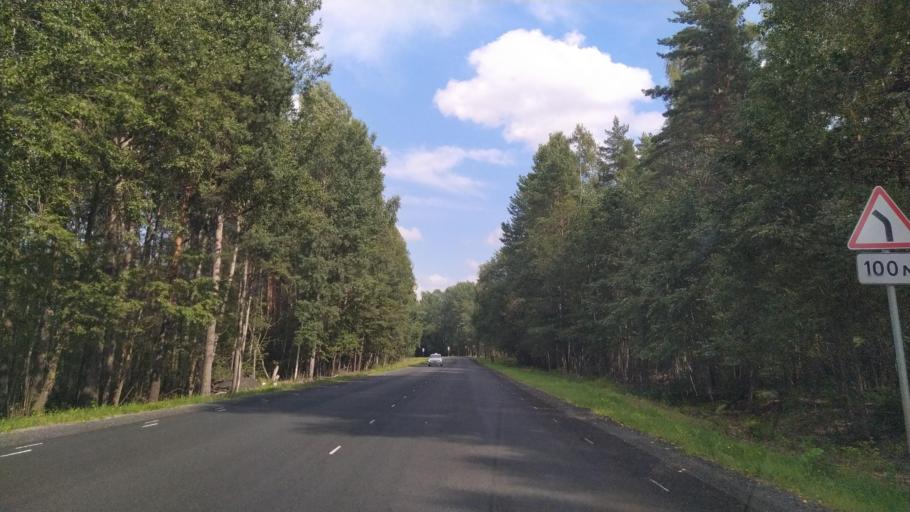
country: RU
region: Pskov
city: Porkhov
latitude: 57.7354
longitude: 29.4088
